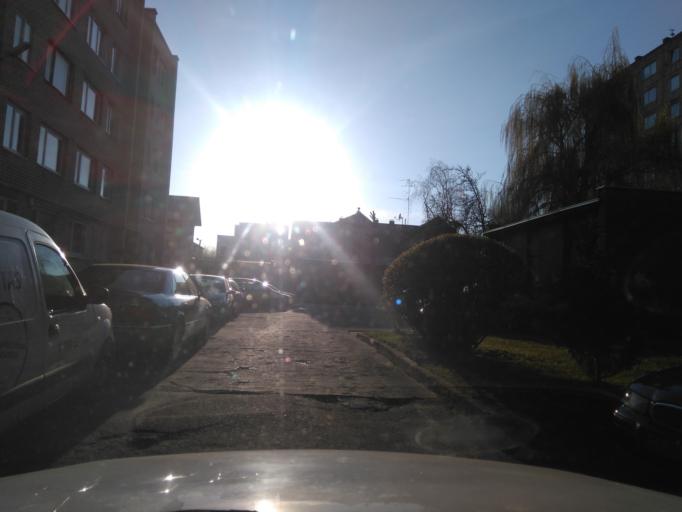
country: LT
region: Kauno apskritis
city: Dainava (Kaunas)
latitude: 54.9113
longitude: 23.9618
